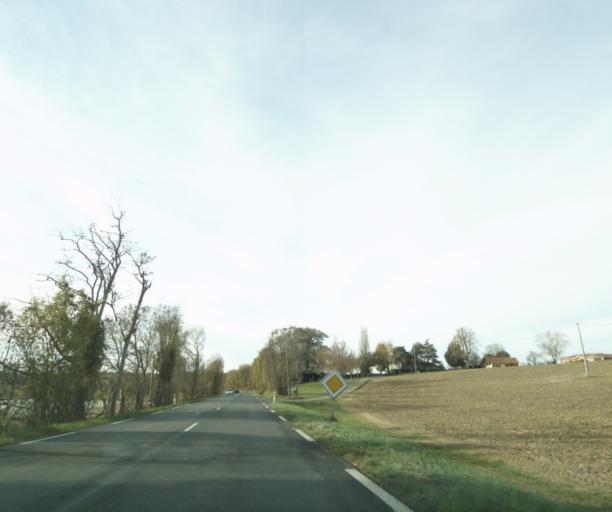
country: FR
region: Midi-Pyrenees
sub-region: Departement du Gers
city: Gimont
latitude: 43.6166
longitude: 0.9304
